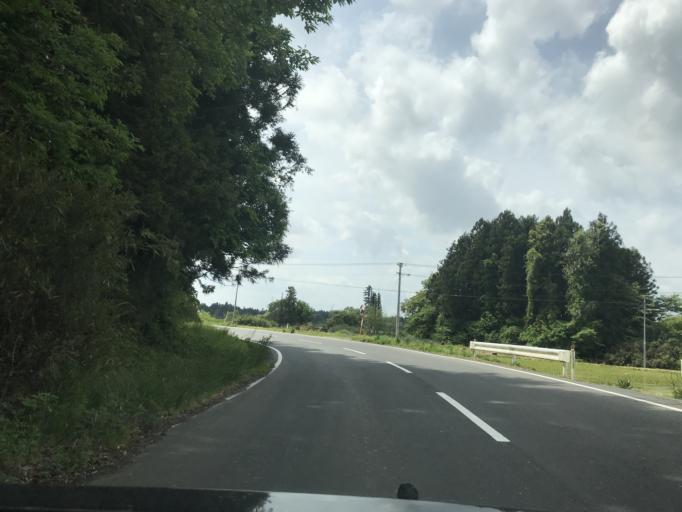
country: JP
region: Iwate
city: Ichinoseki
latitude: 38.8349
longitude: 141.0185
